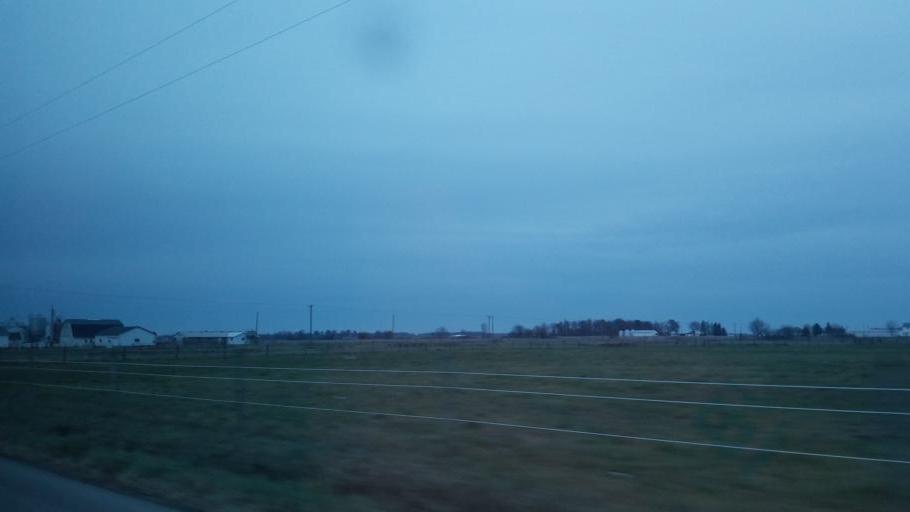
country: US
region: Indiana
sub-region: Adams County
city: Berne
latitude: 40.7299
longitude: -84.8984
